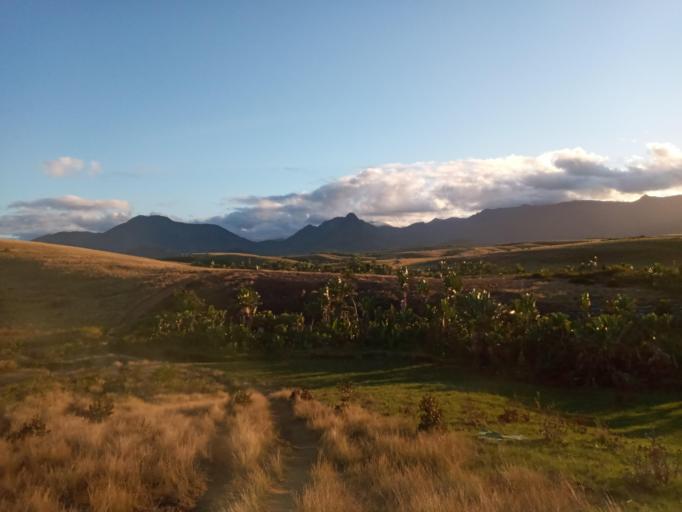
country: MG
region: Anosy
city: Fort Dauphin
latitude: -24.5135
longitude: 47.2507
